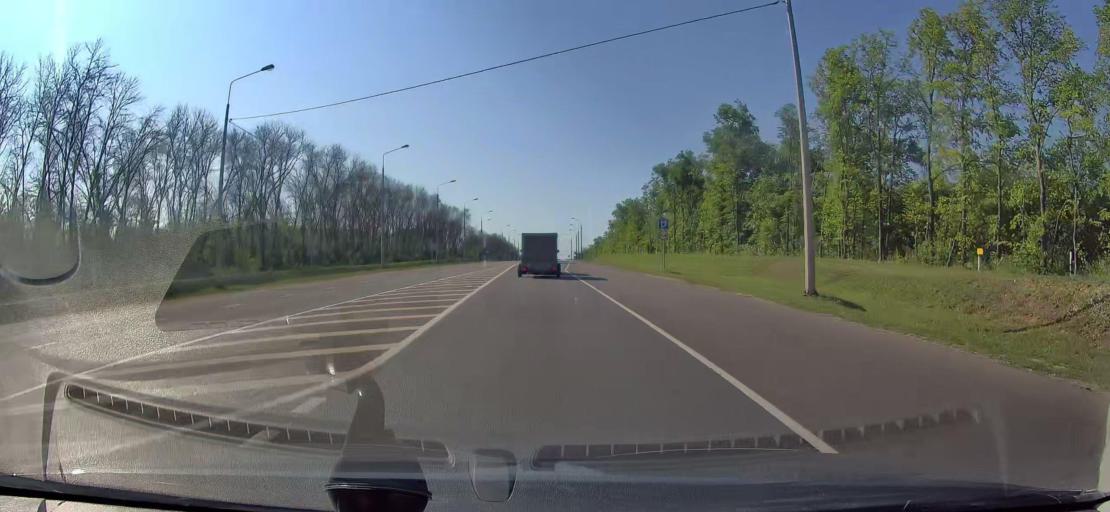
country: RU
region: Orjol
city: Kromy
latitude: 52.6323
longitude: 35.7528
